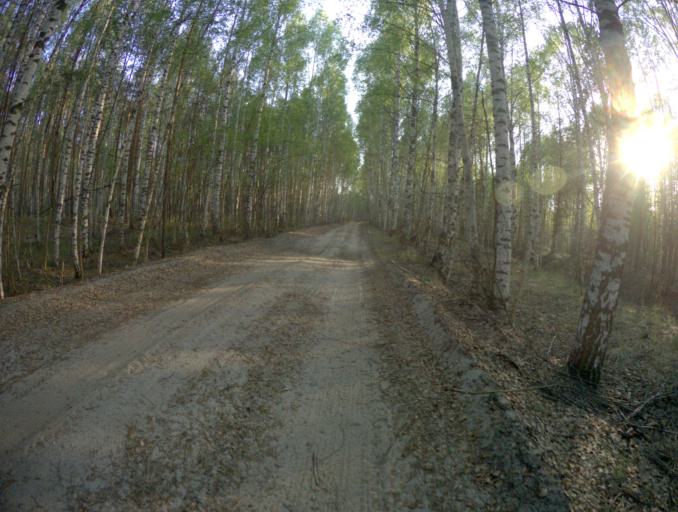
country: RU
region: Vladimir
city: Vyazniki
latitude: 56.3658
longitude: 42.1526
